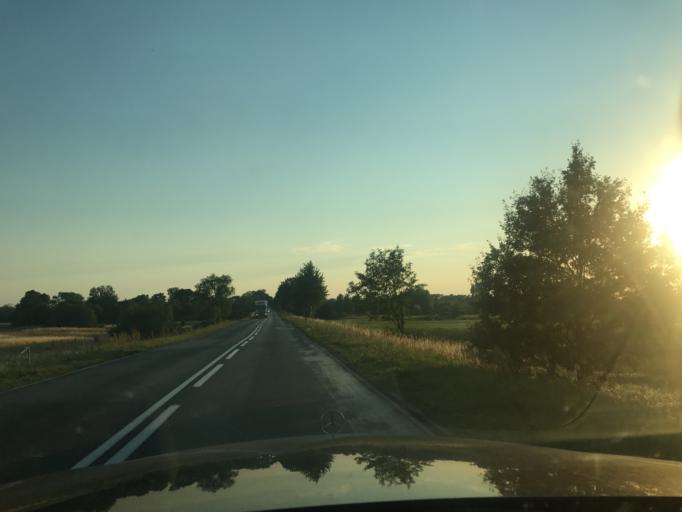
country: PL
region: Lublin Voivodeship
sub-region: Powiat lubartowski
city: Lubartow
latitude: 51.4989
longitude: 22.6505
